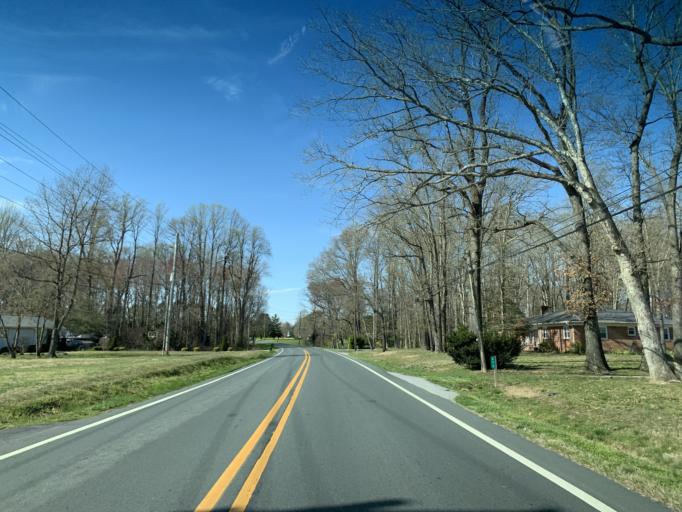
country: US
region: Delaware
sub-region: Sussex County
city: Milford
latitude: 38.9353
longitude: -75.4580
